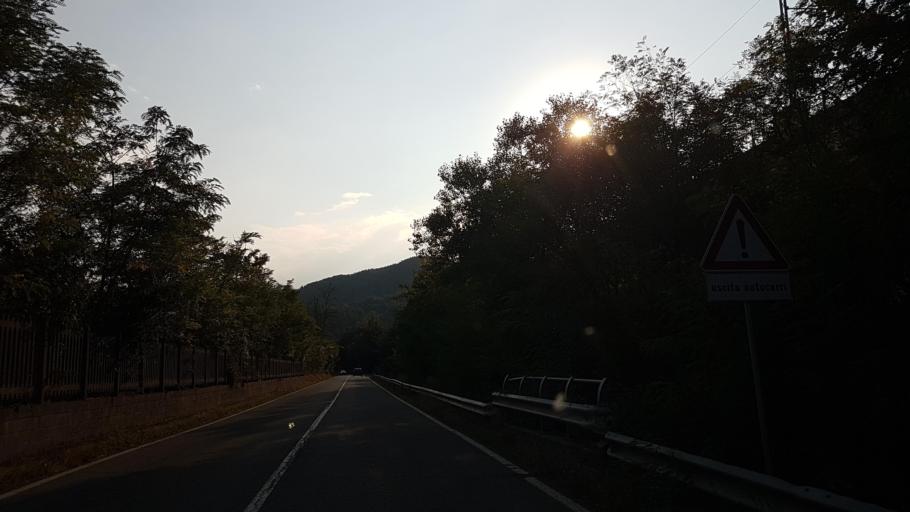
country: IT
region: Emilia-Romagna
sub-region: Provincia di Parma
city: Stazione Valmozzola
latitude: 44.5927
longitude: 9.9528
